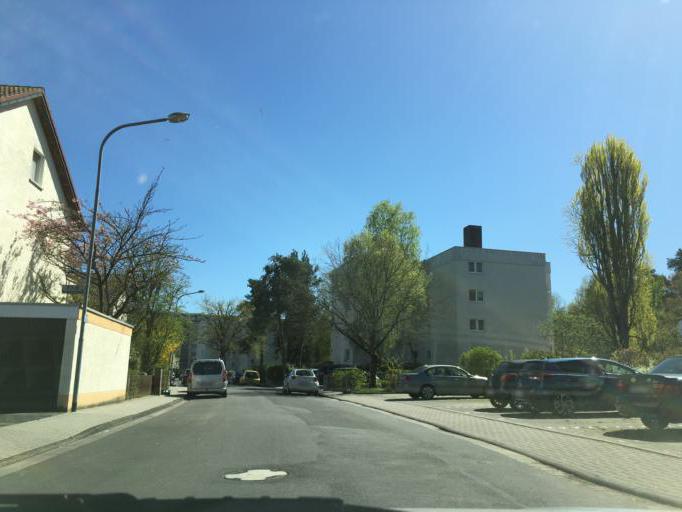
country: DE
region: Hesse
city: Obertshausen
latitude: 50.0802
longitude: 8.8533
